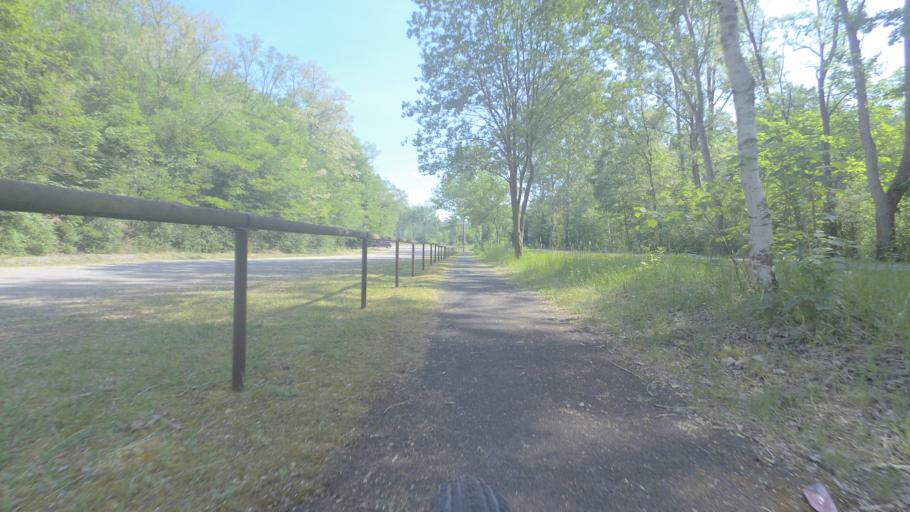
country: DE
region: Saxony-Anhalt
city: Frose
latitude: 51.8296
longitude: 11.3831
